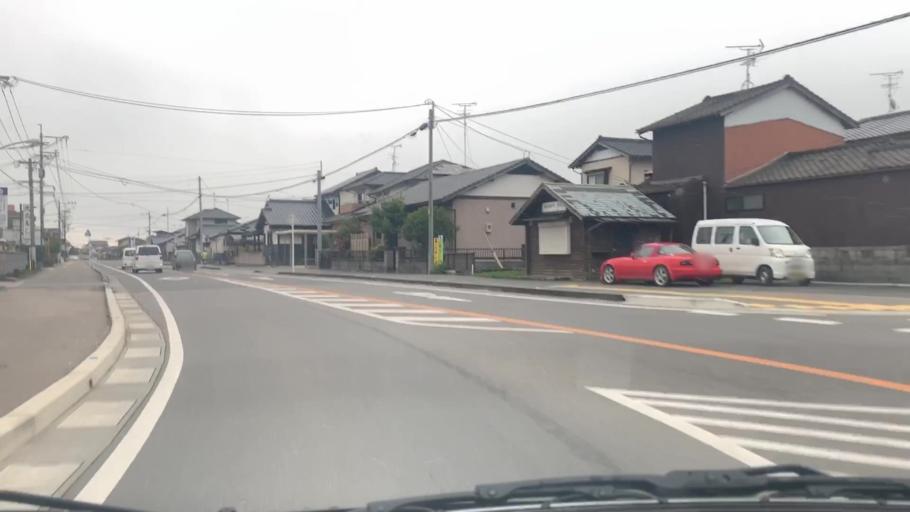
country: JP
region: Saga Prefecture
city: Kashima
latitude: 33.1874
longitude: 130.1362
